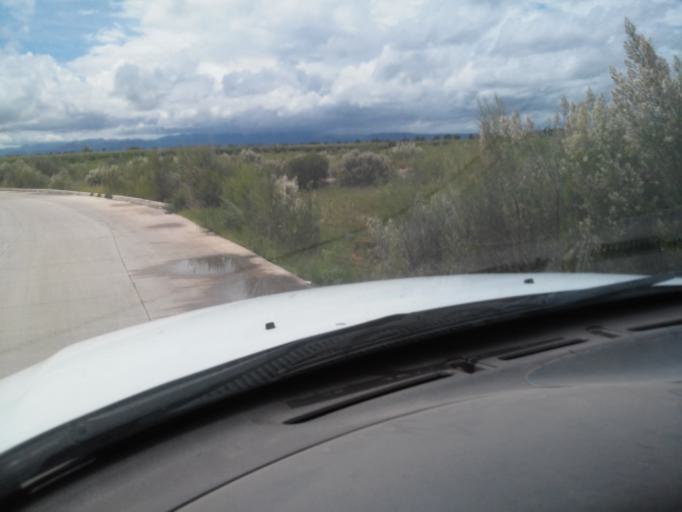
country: MX
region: Durango
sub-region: Durango
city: Jose Refugio Salcido
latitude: 24.0162
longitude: -104.5469
